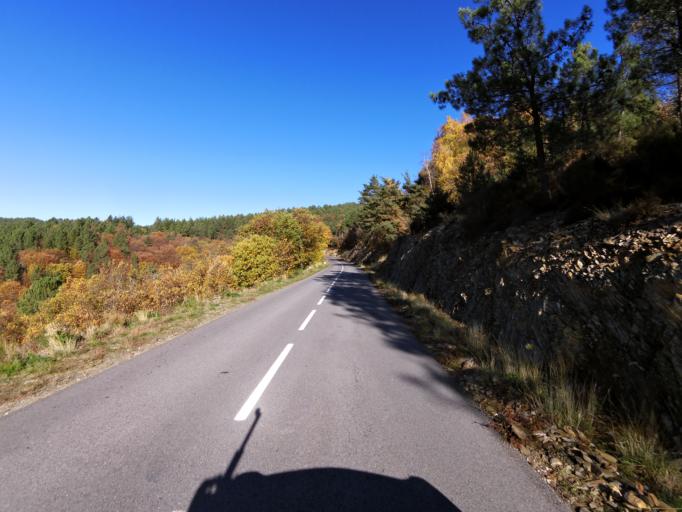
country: FR
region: Rhone-Alpes
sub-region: Departement de l'Ardeche
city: Les Vans
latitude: 44.5011
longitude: 4.1226
